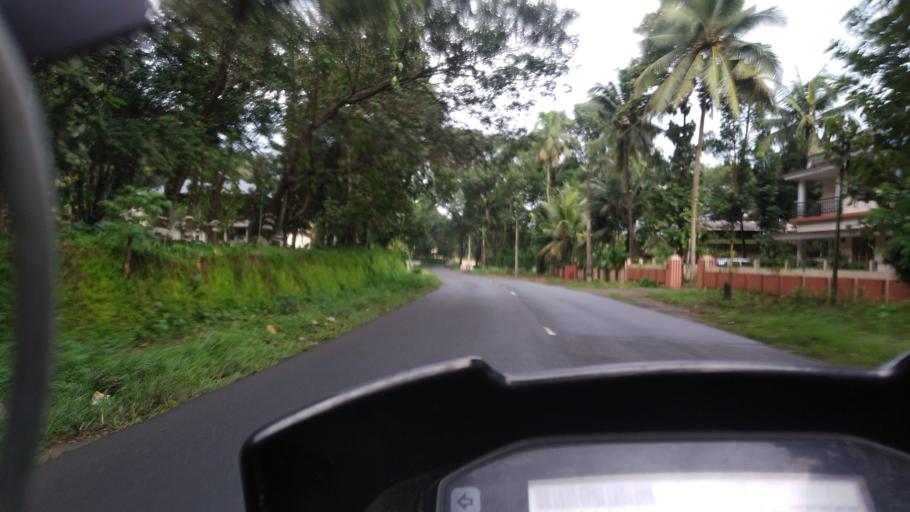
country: IN
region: Kerala
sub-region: Ernakulam
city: Kotamangalam
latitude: 10.0575
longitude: 76.6937
